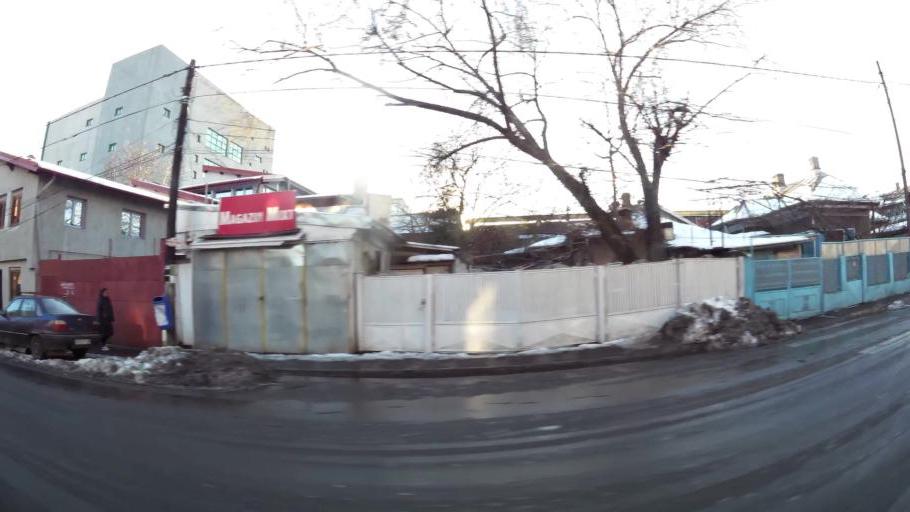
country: RO
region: Ilfov
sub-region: Comuna Fundeni-Dobroesti
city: Fundeni
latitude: 44.4498
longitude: 26.1482
